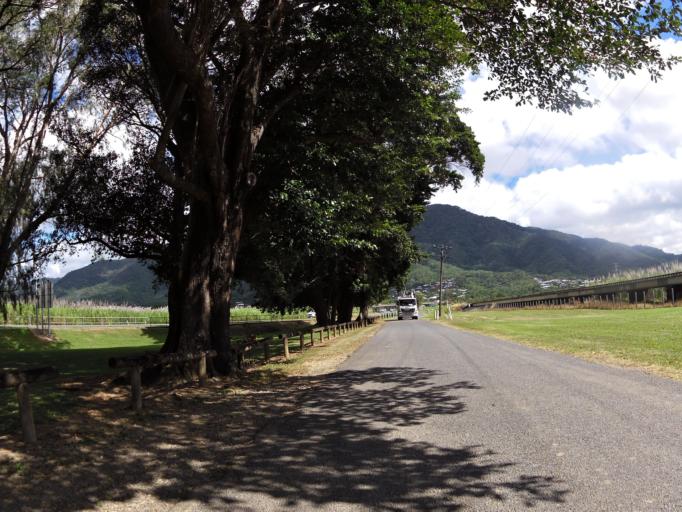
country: AU
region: Queensland
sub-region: Cairns
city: Redlynch
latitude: -16.8848
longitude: 145.7026
